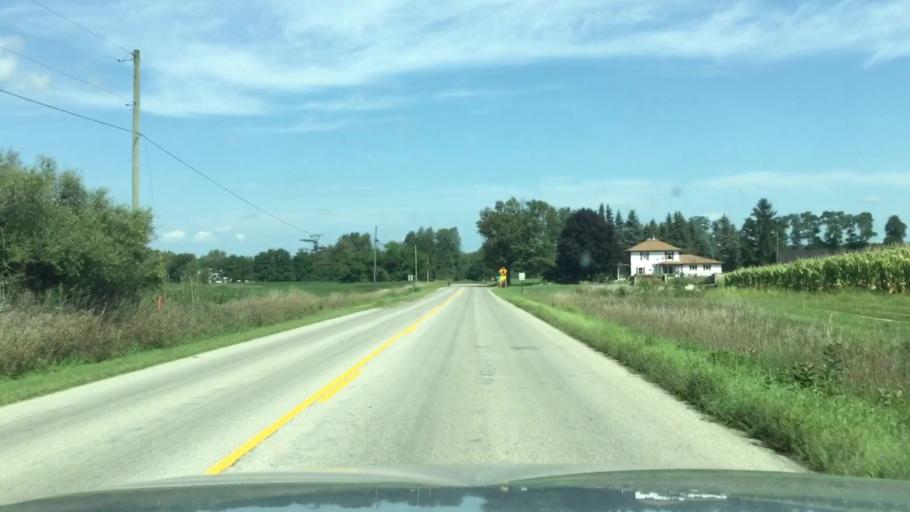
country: US
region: Michigan
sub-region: Jackson County
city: Brooklyn
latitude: 42.0454
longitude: -84.2764
